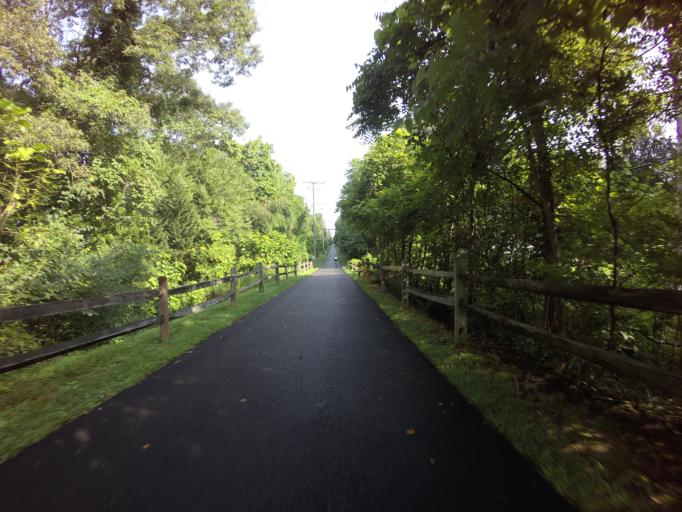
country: US
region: Maryland
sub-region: Anne Arundel County
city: Pasadena
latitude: 39.1091
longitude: -76.5773
